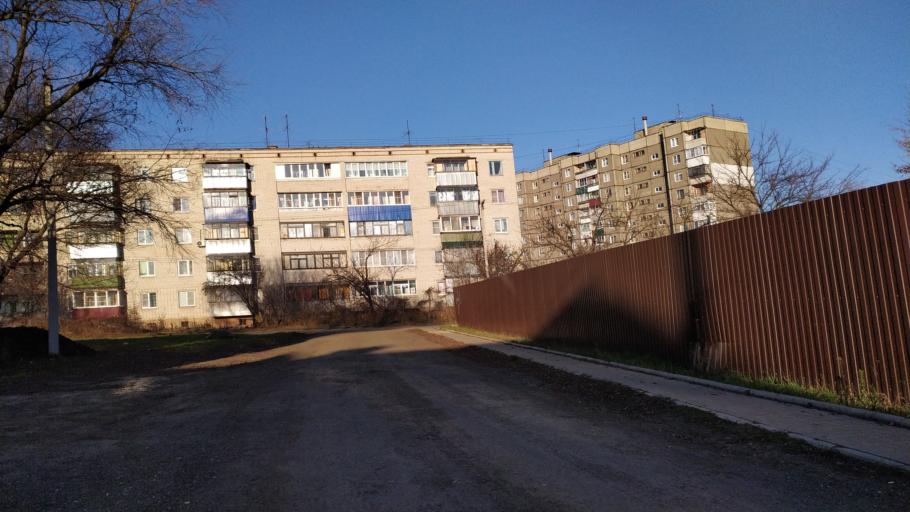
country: RU
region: Kursk
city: Kursk
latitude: 51.6464
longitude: 36.1381
